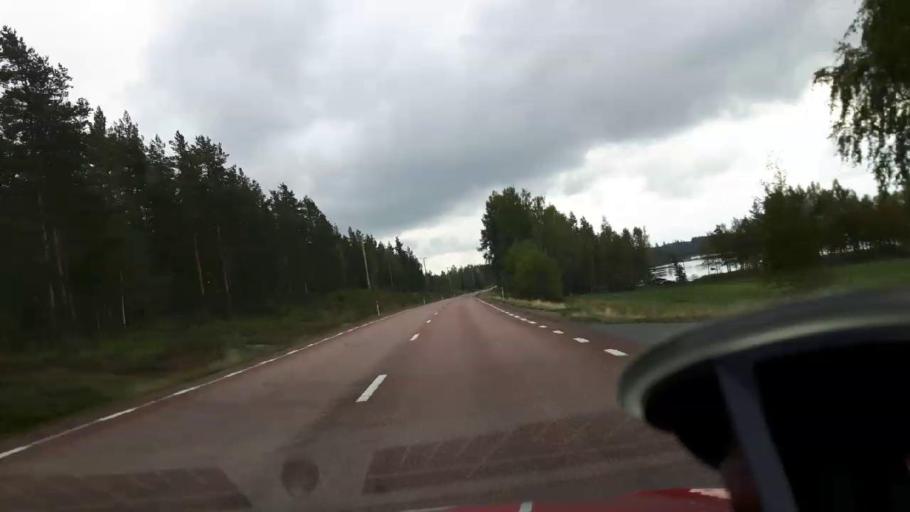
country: SE
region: Gaevleborg
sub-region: Soderhamns Kommun
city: Soderhamn
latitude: 61.1312
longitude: 16.9241
